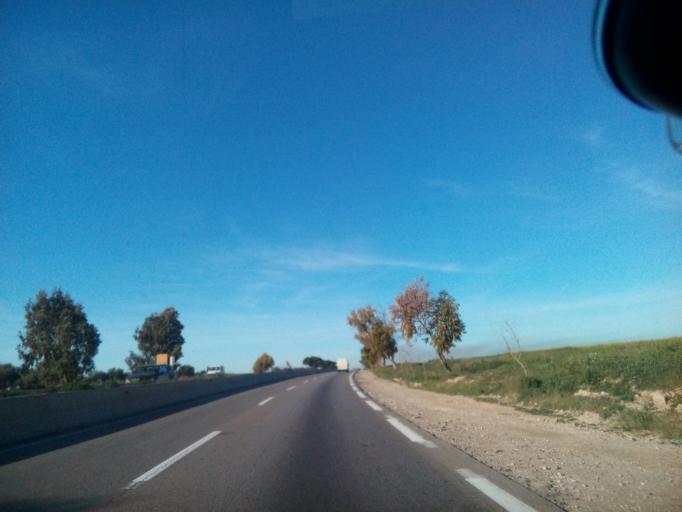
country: DZ
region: Oran
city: Ain el Bya
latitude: 35.7667
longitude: -0.2100
